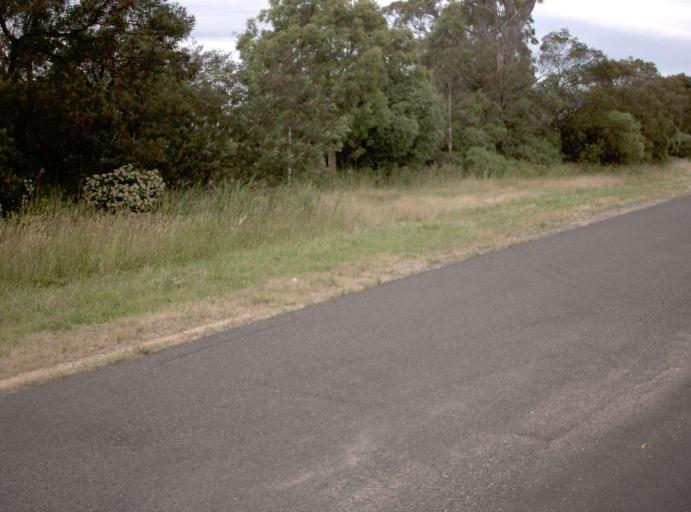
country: AU
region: Victoria
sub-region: East Gippsland
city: Bairnsdale
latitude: -37.8802
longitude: 147.6562
